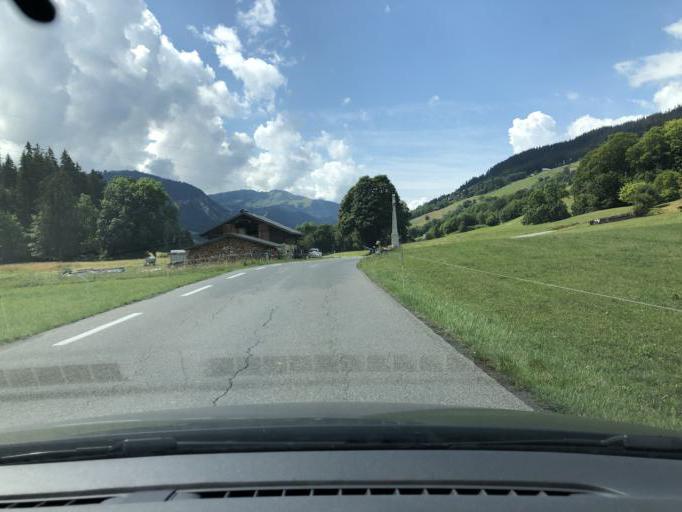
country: FR
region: Rhone-Alpes
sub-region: Departement de la Haute-Savoie
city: Combloux
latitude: 45.8759
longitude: 6.6257
